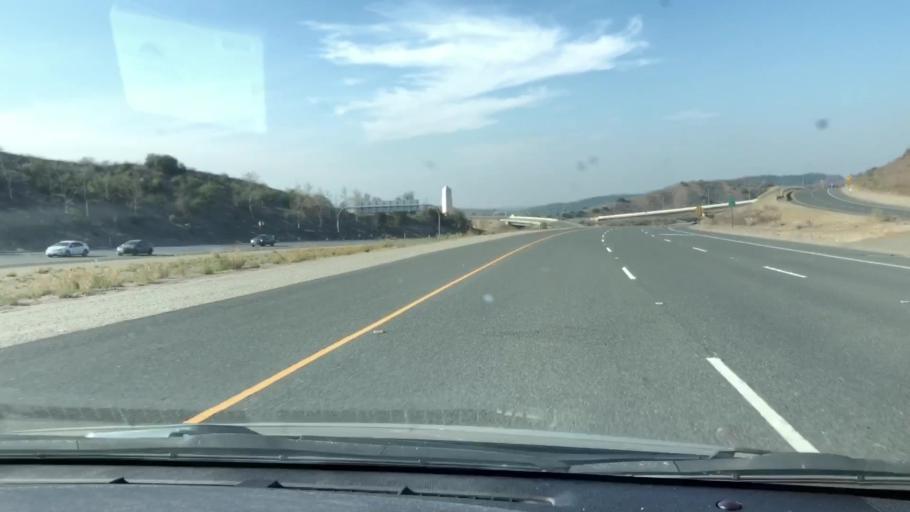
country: US
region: California
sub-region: Orange County
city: Foothill Ranch
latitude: 33.7075
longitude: -117.7163
